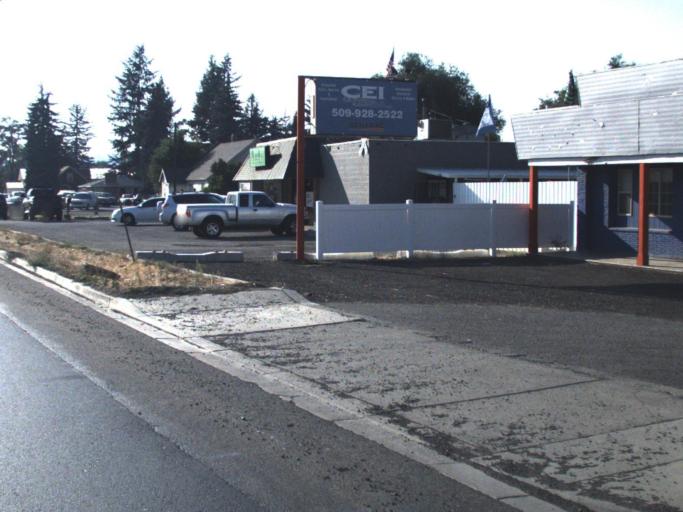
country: US
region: Washington
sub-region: Spokane County
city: Trentwood
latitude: 47.6952
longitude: -117.2038
